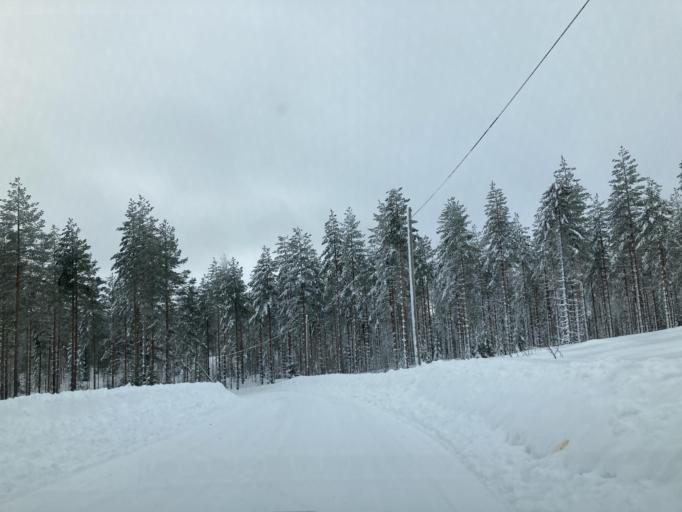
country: FI
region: Central Finland
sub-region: Jaemsae
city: Jaemsae
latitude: 61.8816
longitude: 25.3229
